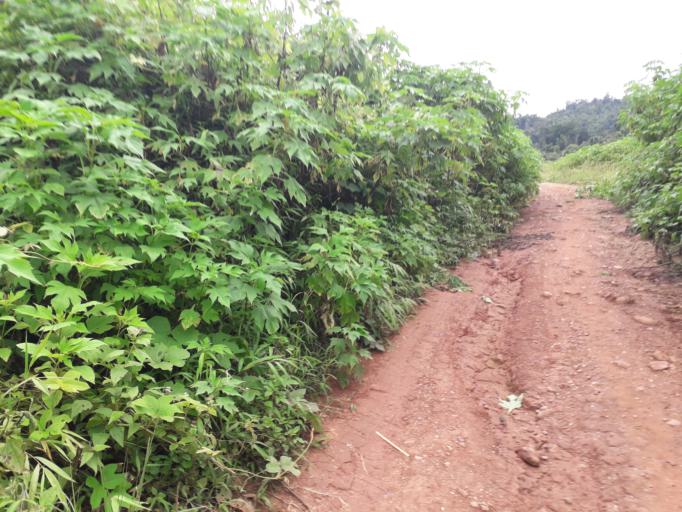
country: CN
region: Yunnan
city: Menglie
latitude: 22.2037
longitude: 101.6672
